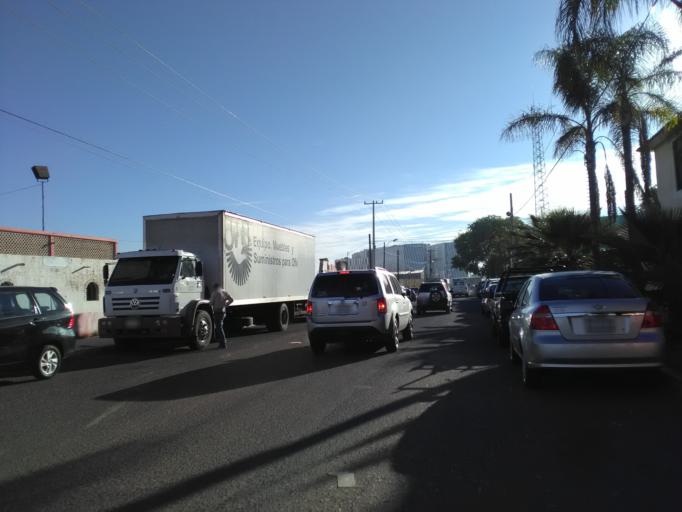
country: MX
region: Durango
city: Victoria de Durango
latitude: 24.0437
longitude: -104.6606
